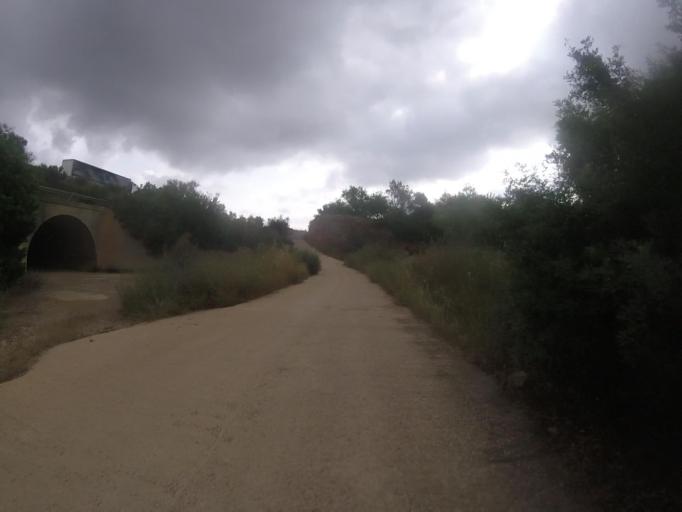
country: ES
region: Valencia
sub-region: Provincia de Castello
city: Santa Magdalena de Pulpis
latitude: 40.3439
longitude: 0.2783
